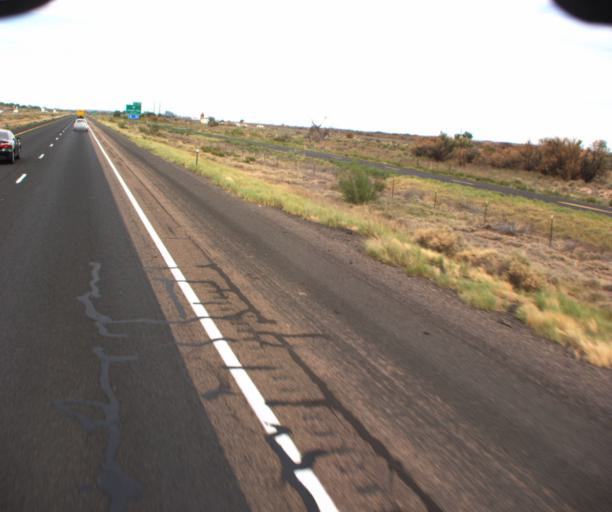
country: US
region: Arizona
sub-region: Navajo County
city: Joseph City
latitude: 34.9587
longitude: -110.3680
